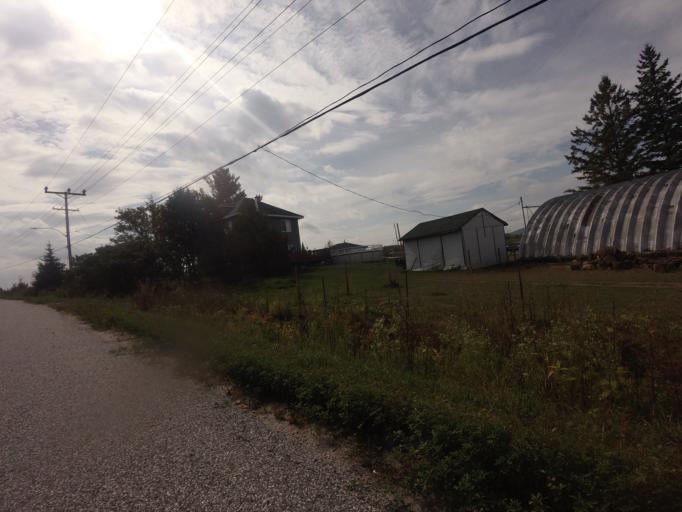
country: CA
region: Quebec
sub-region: Outaouais
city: Wakefield
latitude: 45.8642
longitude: -76.0210
